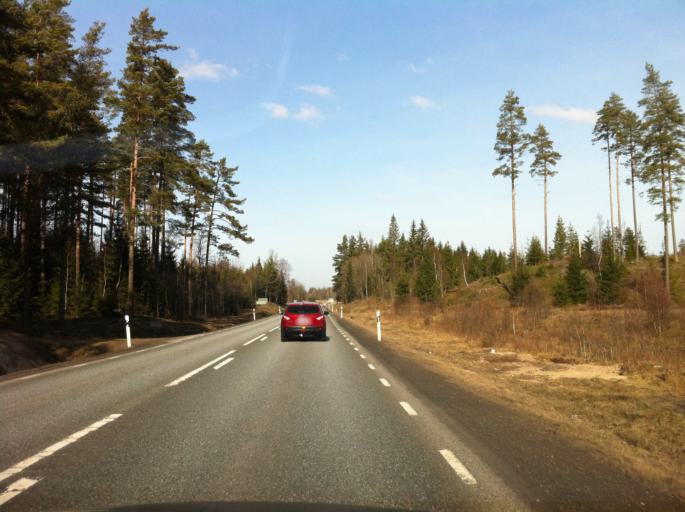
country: SE
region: Joenkoeping
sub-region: Mullsjo Kommun
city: Mullsjoe
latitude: 57.9867
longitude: 13.8282
